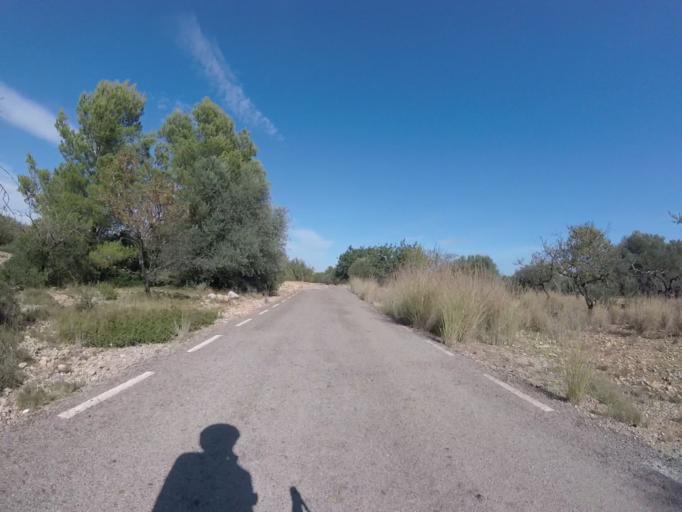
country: ES
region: Valencia
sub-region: Provincia de Castello
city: Sarratella
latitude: 40.2733
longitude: 0.0602
